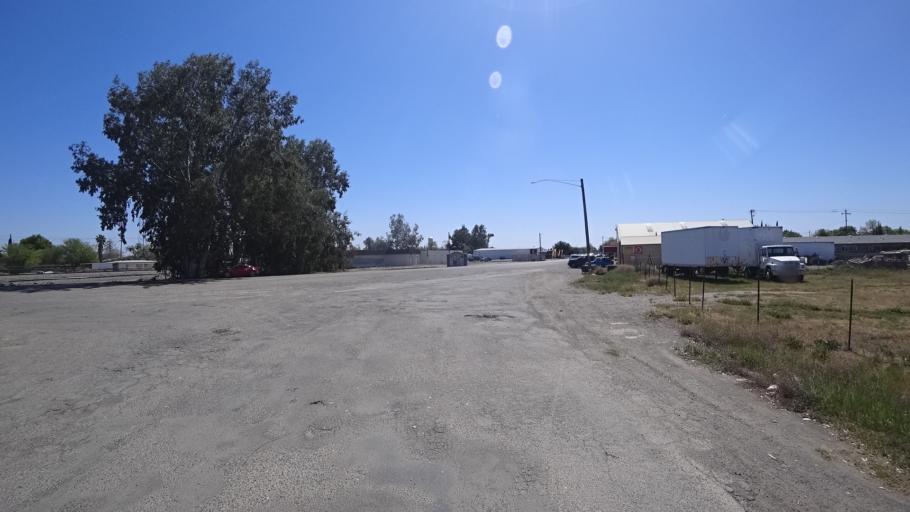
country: US
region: California
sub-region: Glenn County
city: Willows
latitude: 39.5277
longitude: -122.1941
